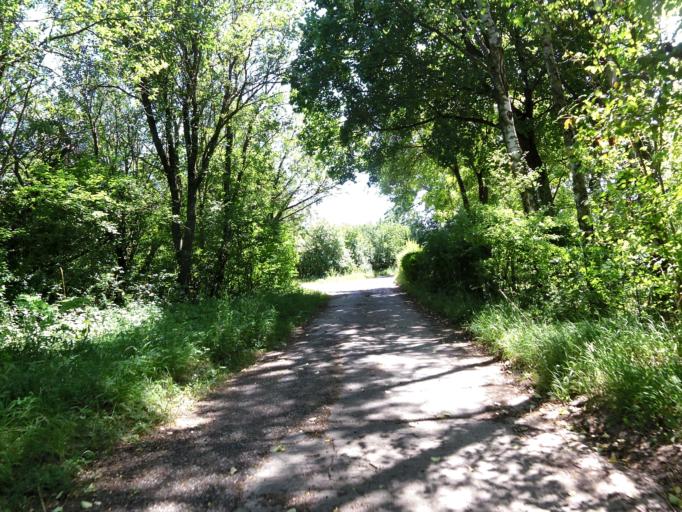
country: DE
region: Bavaria
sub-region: Regierungsbezirk Unterfranken
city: Randersacker
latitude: 49.7606
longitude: 9.9971
